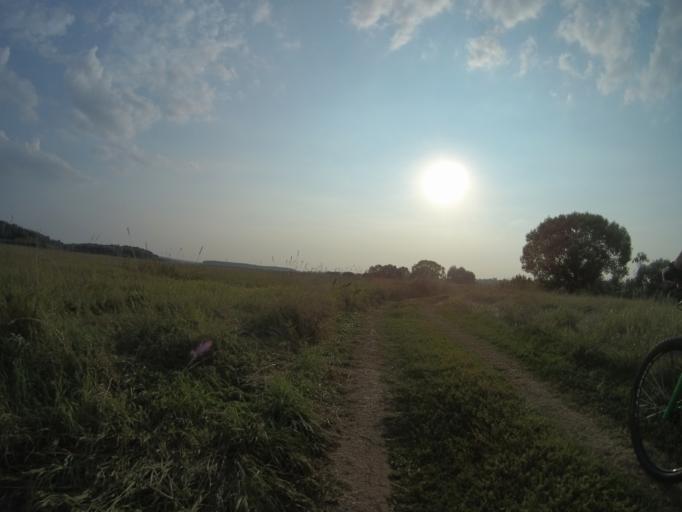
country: RU
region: Vladimir
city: Orgtrud
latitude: 56.3046
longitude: 40.6450
